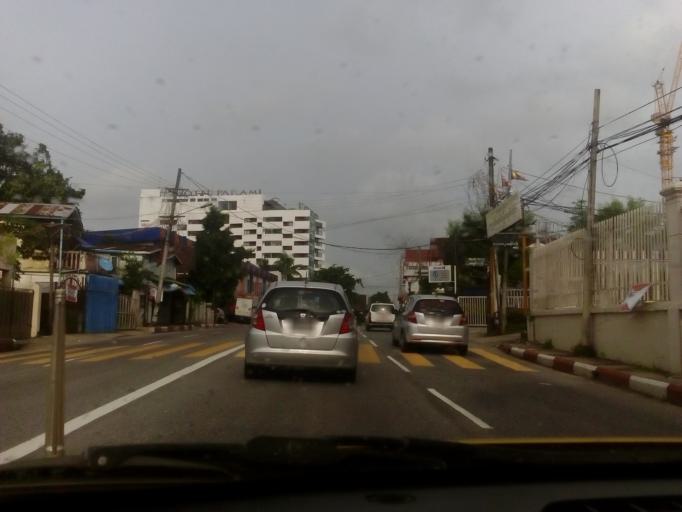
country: MM
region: Yangon
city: Yangon
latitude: 16.8520
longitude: 96.1497
